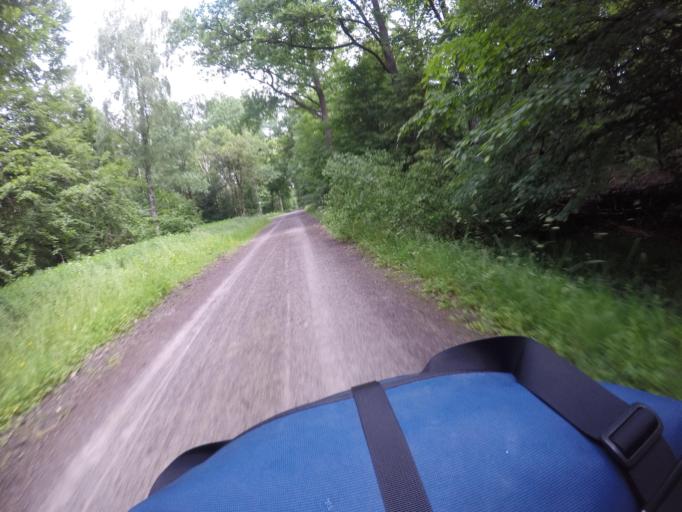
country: DE
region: Baden-Wuerttemberg
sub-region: Regierungsbezirk Stuttgart
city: Gerlingen
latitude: 48.7602
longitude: 9.0815
